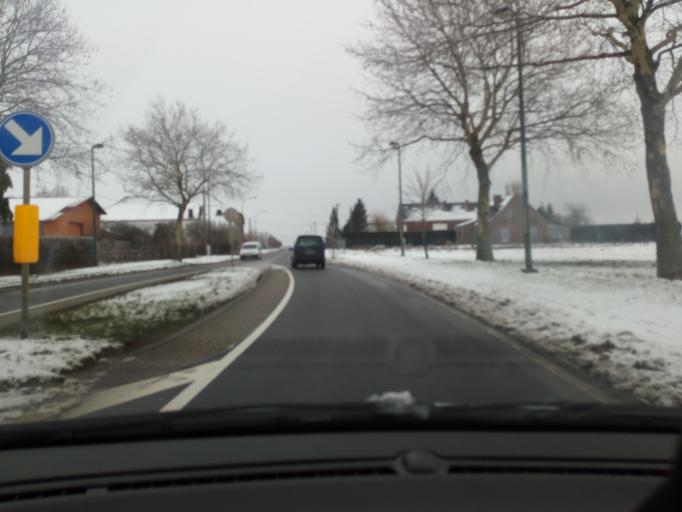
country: BE
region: Wallonia
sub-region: Province du Hainaut
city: Binche
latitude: 50.4110
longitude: 4.1361
